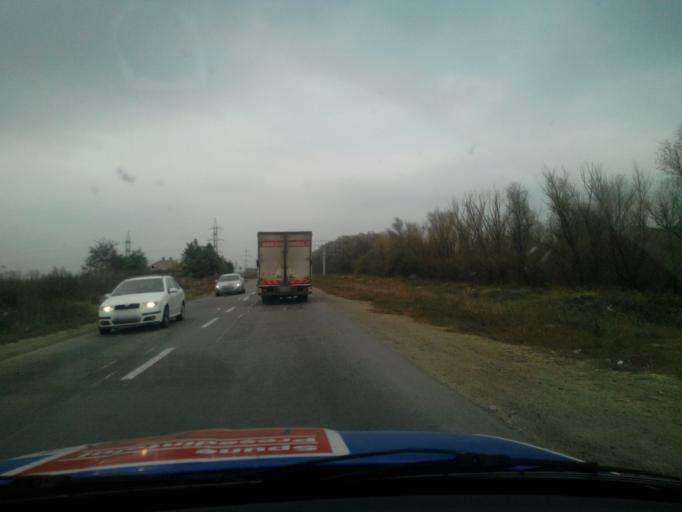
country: RO
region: Braila
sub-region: Municipiul Braila
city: Braila
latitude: 45.3034
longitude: 27.9820
